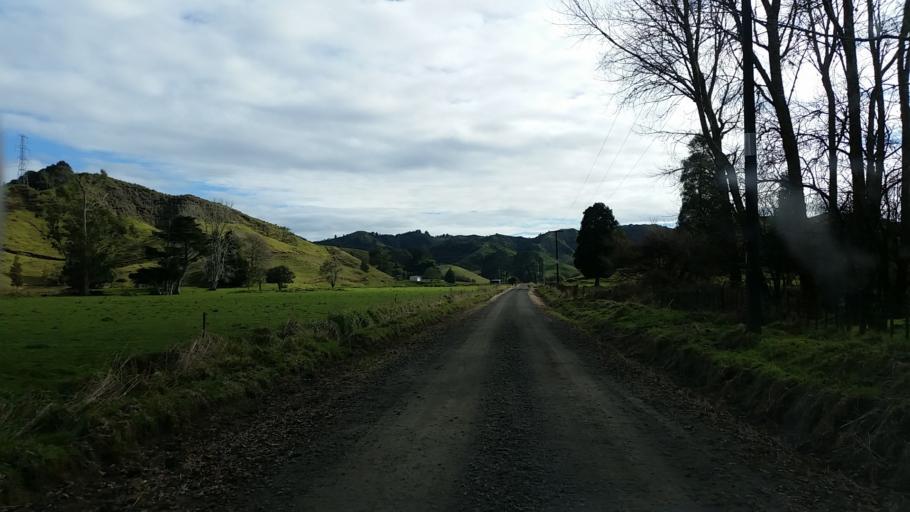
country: NZ
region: Taranaki
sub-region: South Taranaki District
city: Eltham
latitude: -39.2343
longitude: 174.5687
